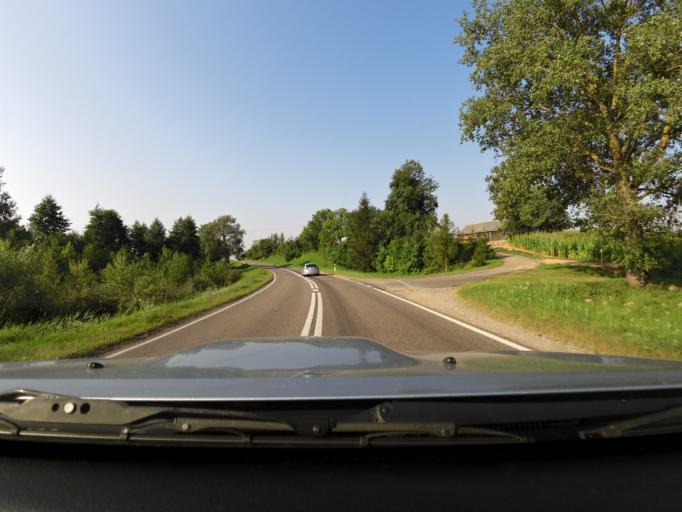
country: PL
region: Podlasie
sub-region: Powiat sejnenski
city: Sejny
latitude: 54.1218
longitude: 23.4314
